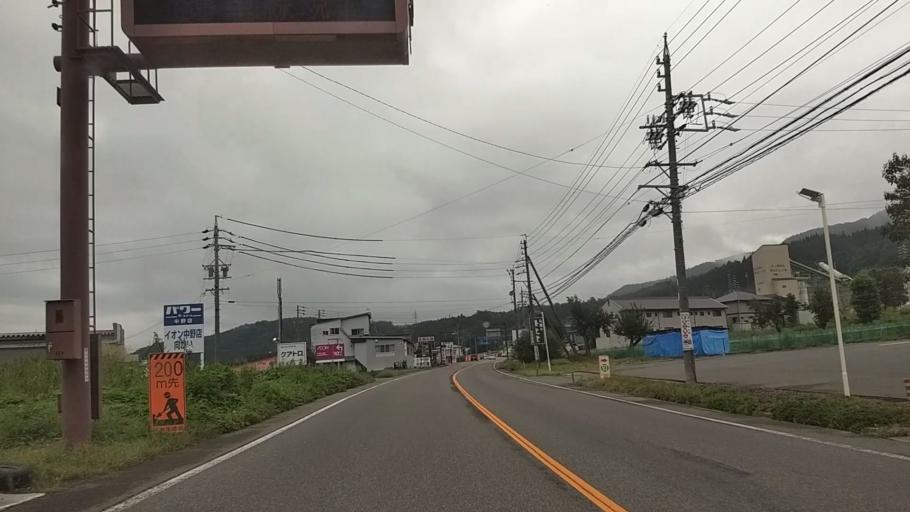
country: JP
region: Nagano
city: Iiyama
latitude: 36.8256
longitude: 138.3531
